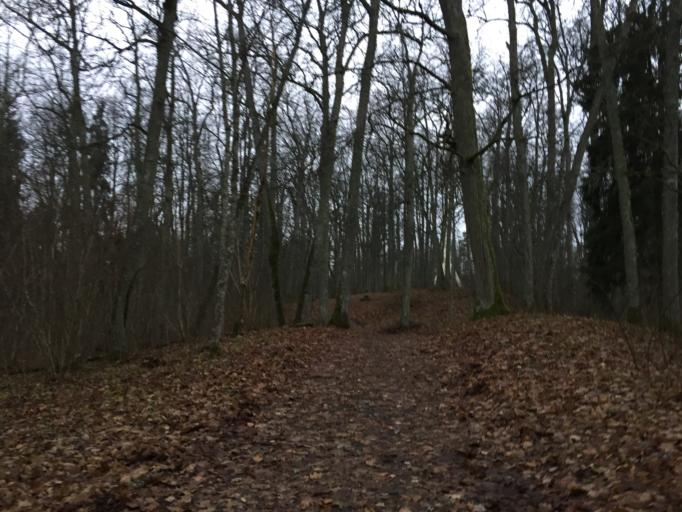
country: LV
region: Koceni
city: Koceni
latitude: 57.5529
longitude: 25.2185
